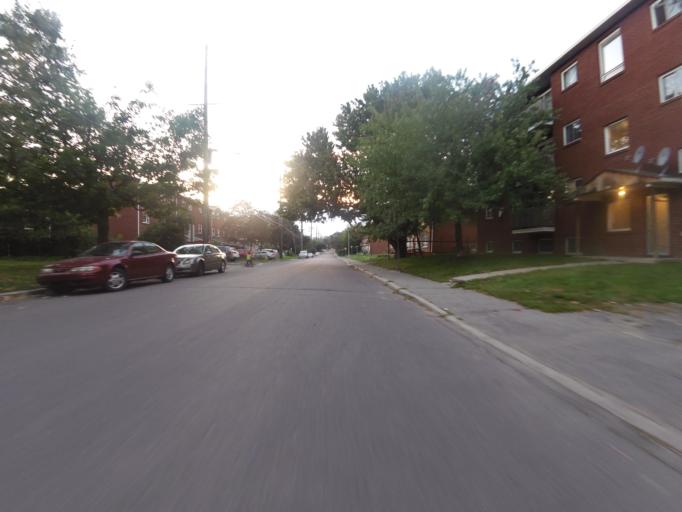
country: CA
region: Ontario
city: Ottawa
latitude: 45.4230
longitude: -75.6564
